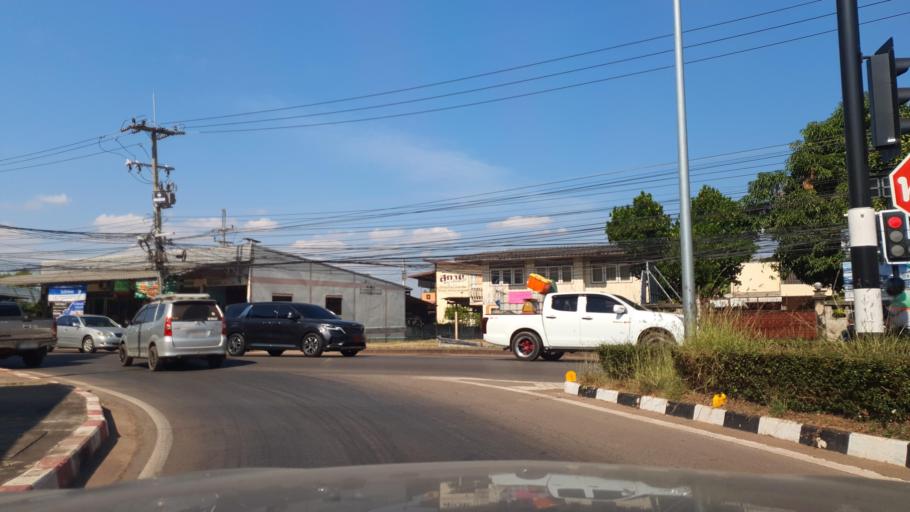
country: TH
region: Sakon Nakhon
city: Sakon Nakhon
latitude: 17.1615
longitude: 104.1275
